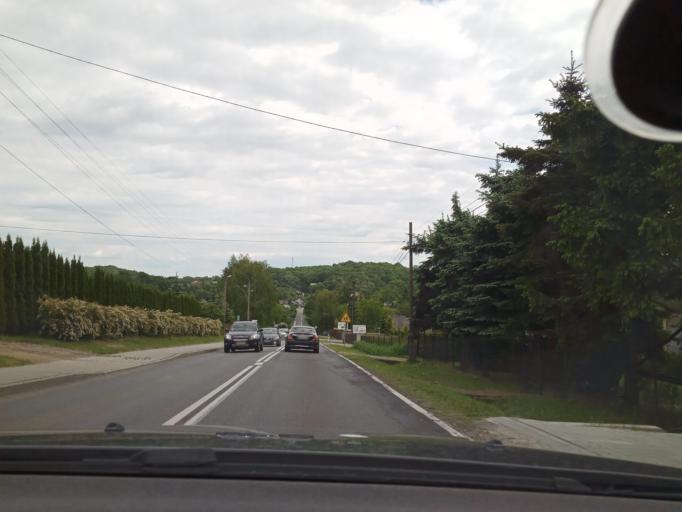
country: PL
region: Lesser Poland Voivodeship
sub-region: Powiat wielicki
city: Tomaszkowice
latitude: 49.9754
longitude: 20.1019
